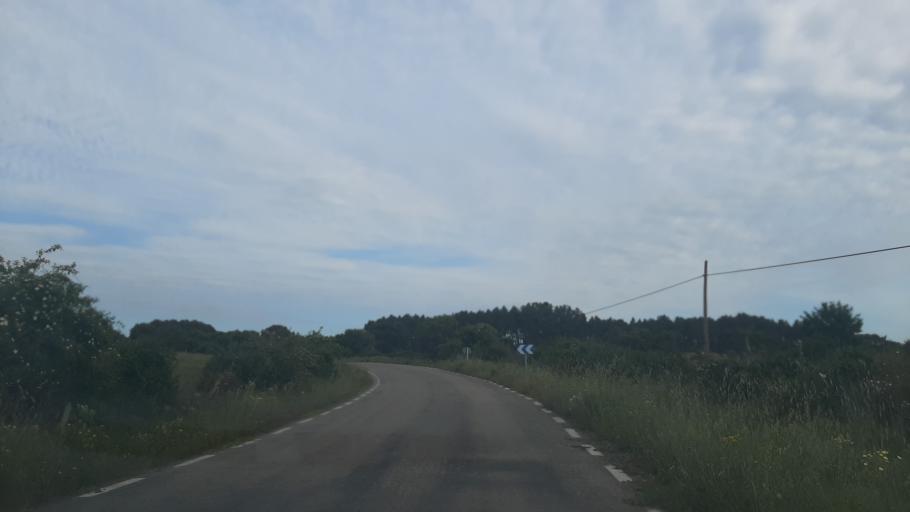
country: ES
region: Castille and Leon
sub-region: Provincia de Salamanca
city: Gallegos de Arganan
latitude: 40.6408
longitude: -6.7310
